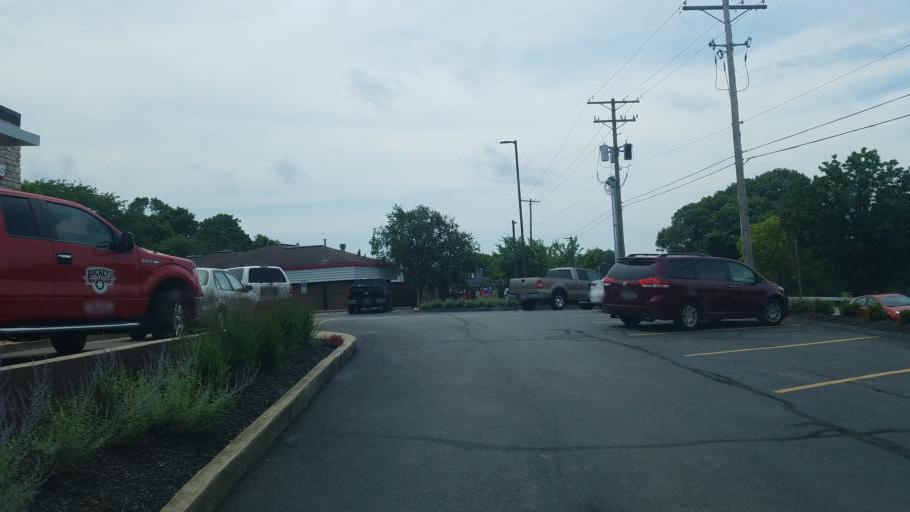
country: US
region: Ohio
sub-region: Franklin County
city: Upper Arlington
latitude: 40.0280
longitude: -83.0911
